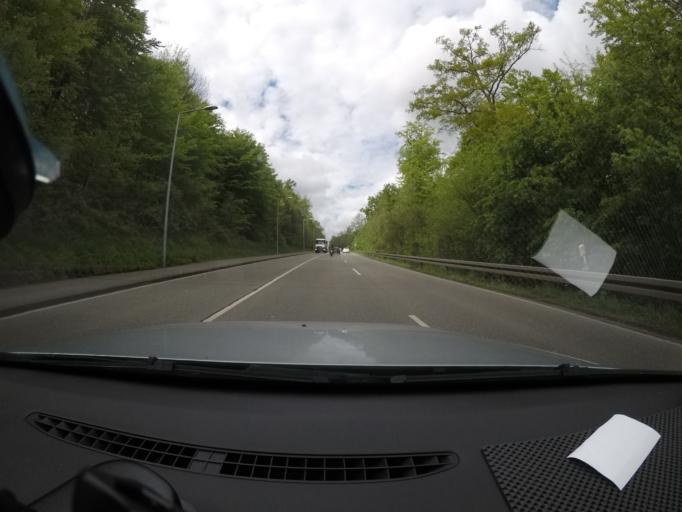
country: DE
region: Baden-Wuerttemberg
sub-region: Regierungsbezirk Stuttgart
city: Stuttgart
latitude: 48.7656
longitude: 9.1385
